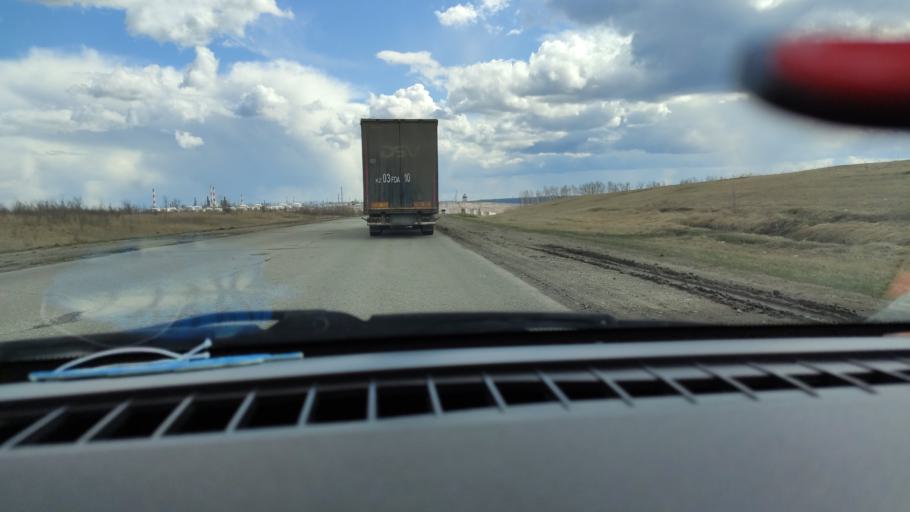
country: RU
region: Samara
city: Varlamovo
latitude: 53.1078
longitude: 48.3563
